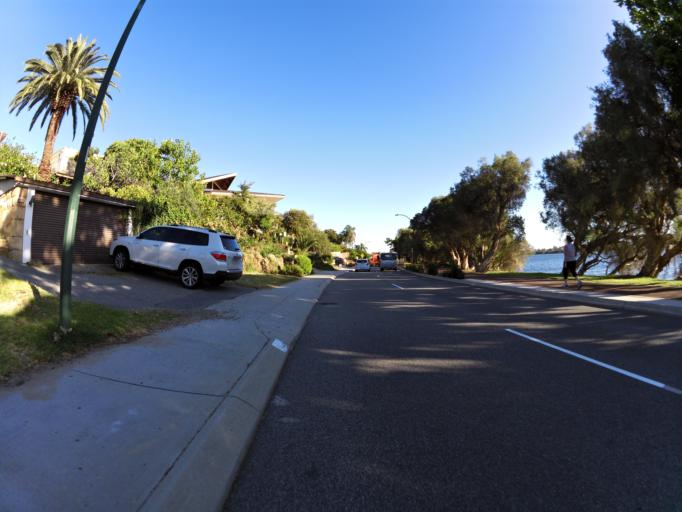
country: AU
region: Western Australia
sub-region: Melville
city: Mount Pleasant
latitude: -32.0330
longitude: 115.8533
